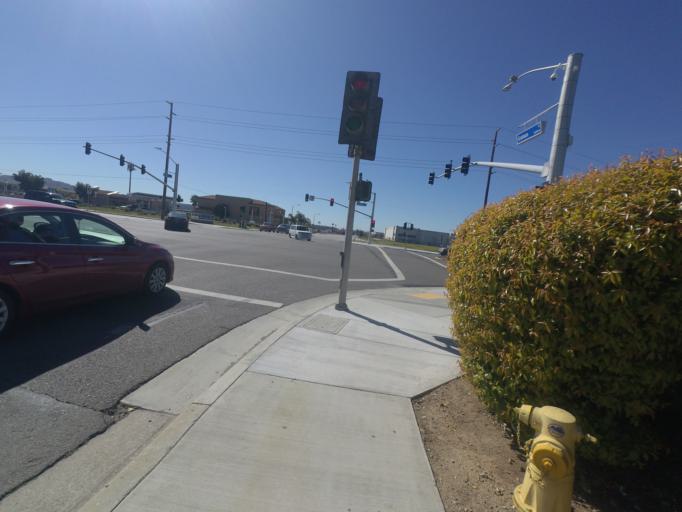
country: US
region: California
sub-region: Riverside County
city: March Air Force Base
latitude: 33.9176
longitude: -117.2525
